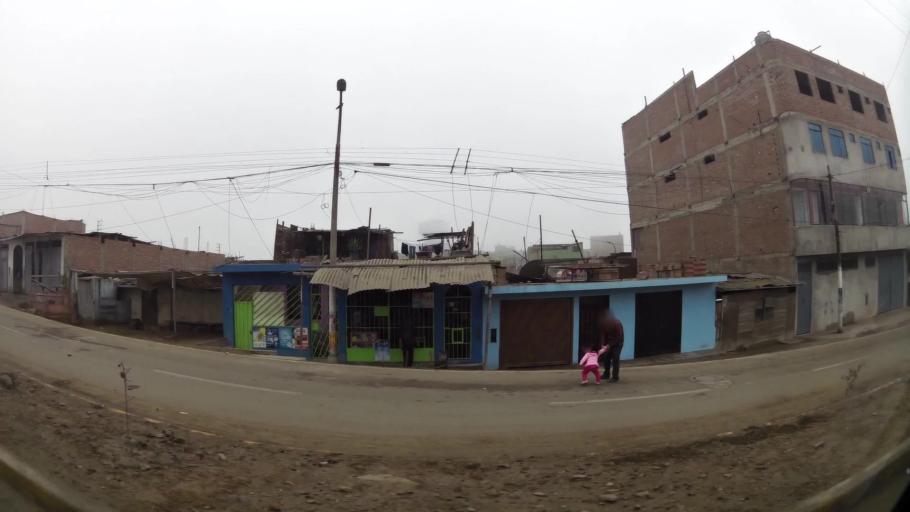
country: PE
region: Lima
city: Ventanilla
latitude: -11.8300
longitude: -77.1048
